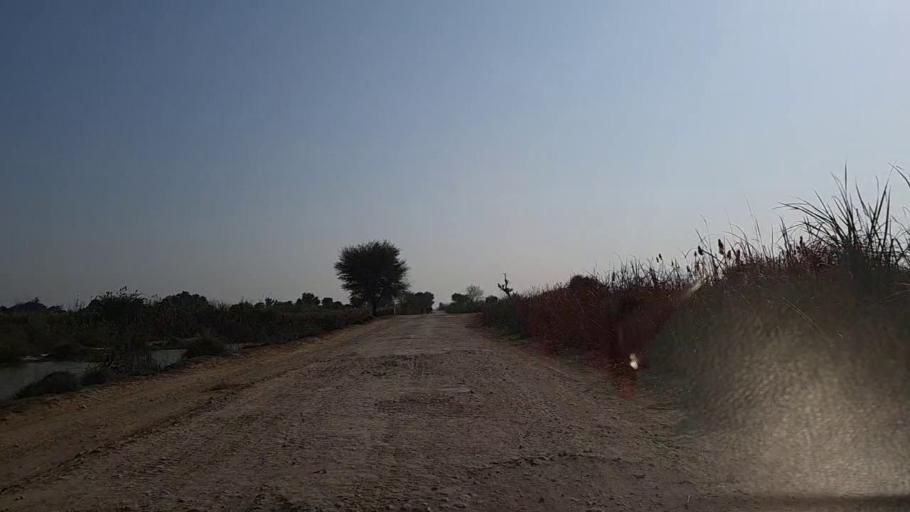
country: PK
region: Sindh
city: Tando Mittha Khan
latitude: 25.9012
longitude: 69.0771
